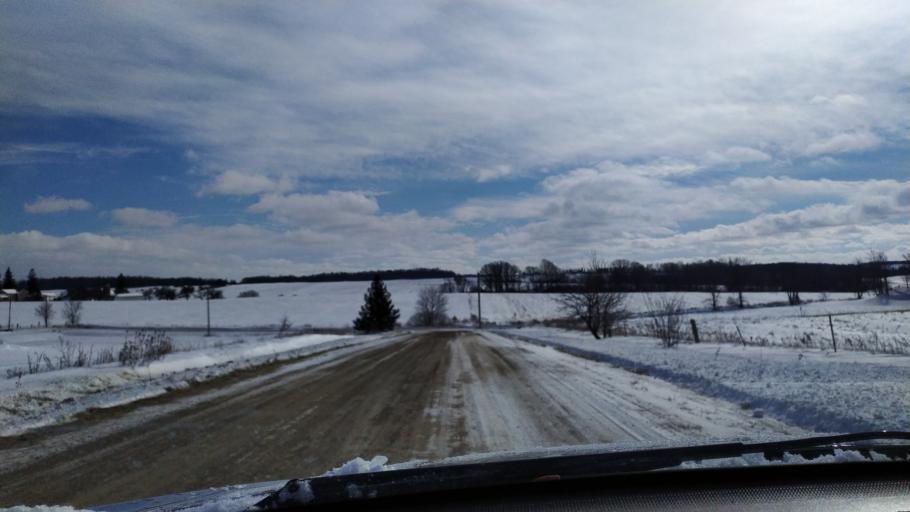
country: CA
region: Ontario
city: Waterloo
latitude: 43.4699
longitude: -80.7384
